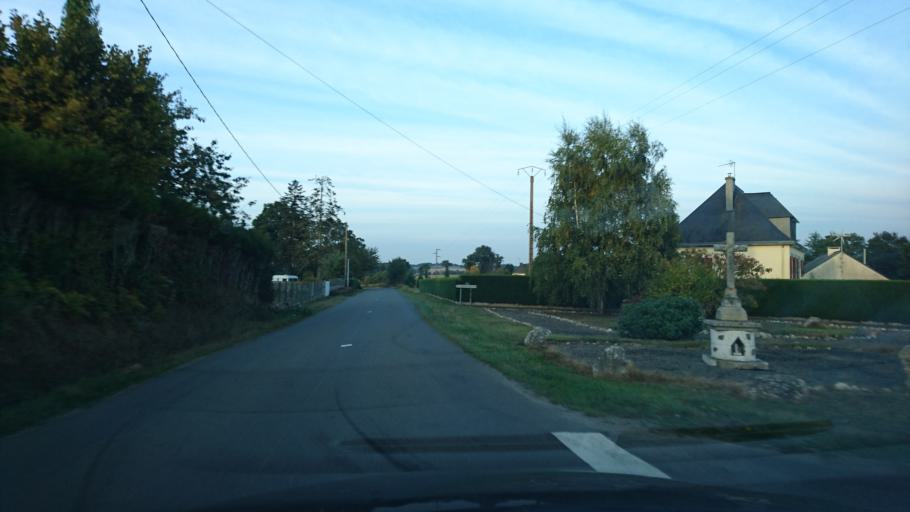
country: FR
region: Brittany
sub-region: Departement d'Ille-et-Vilaine
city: Sixt-sur-Aff
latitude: 47.7899
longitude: -2.0645
